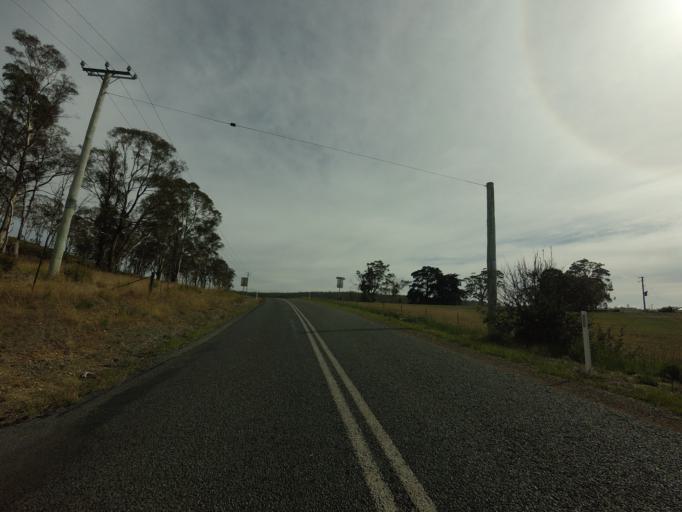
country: AU
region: Tasmania
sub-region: Brighton
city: Bridgewater
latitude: -42.3435
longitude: 147.4045
